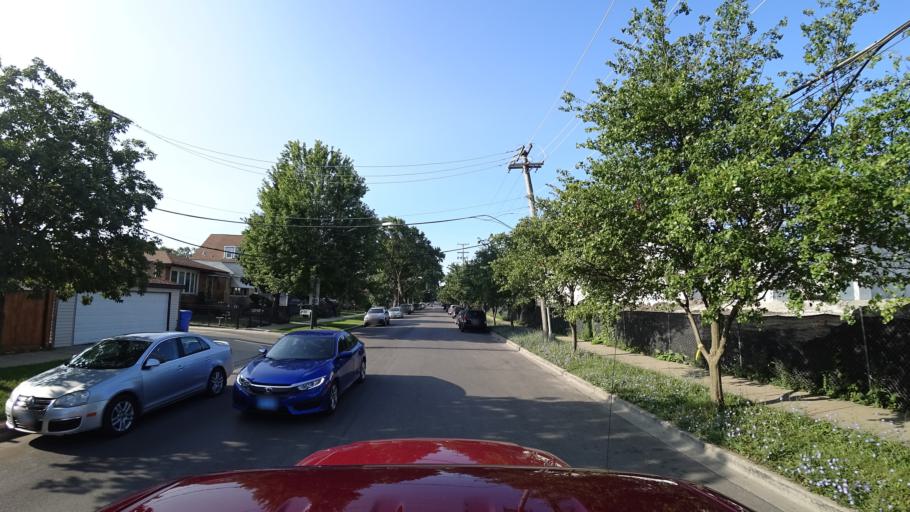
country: US
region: Illinois
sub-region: Cook County
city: Cicero
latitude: 41.8005
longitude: -87.7112
